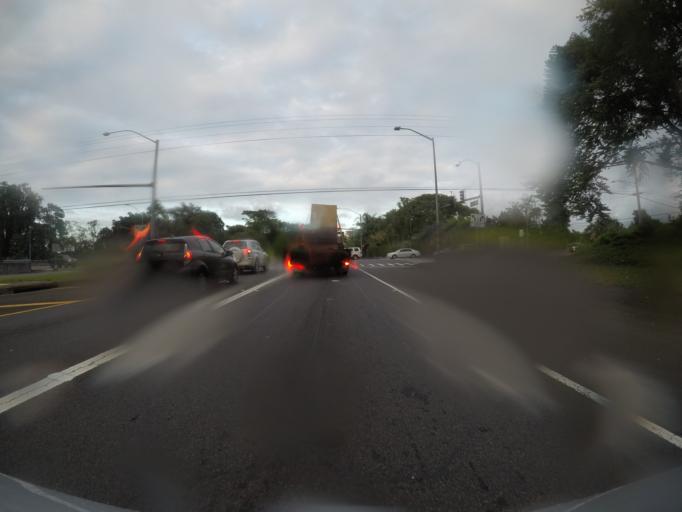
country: US
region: Hawaii
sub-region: Hawaii County
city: Hilo
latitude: 19.6938
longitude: -155.0909
